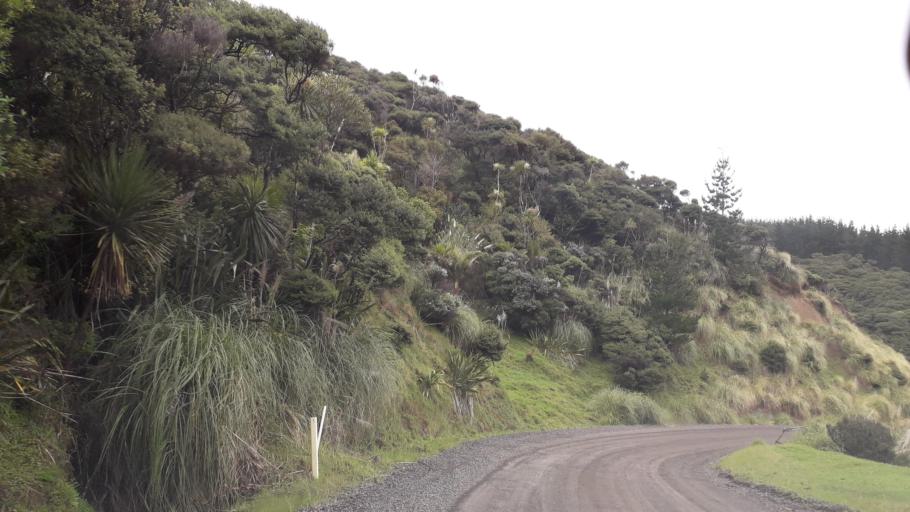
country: NZ
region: Northland
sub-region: Far North District
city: Ahipara
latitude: -35.4399
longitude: 173.3041
